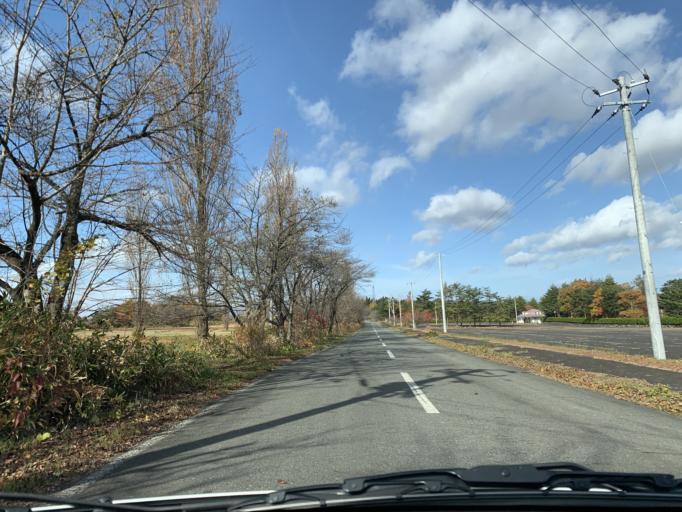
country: JP
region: Iwate
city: Mizusawa
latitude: 39.0336
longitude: 141.0857
